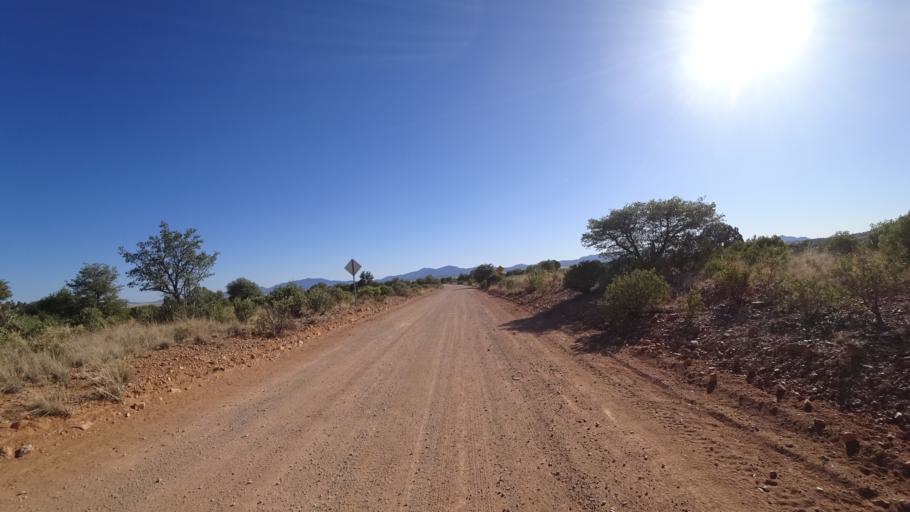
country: MX
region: Sonora
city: Santa Cruz
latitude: 31.4838
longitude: -110.5612
